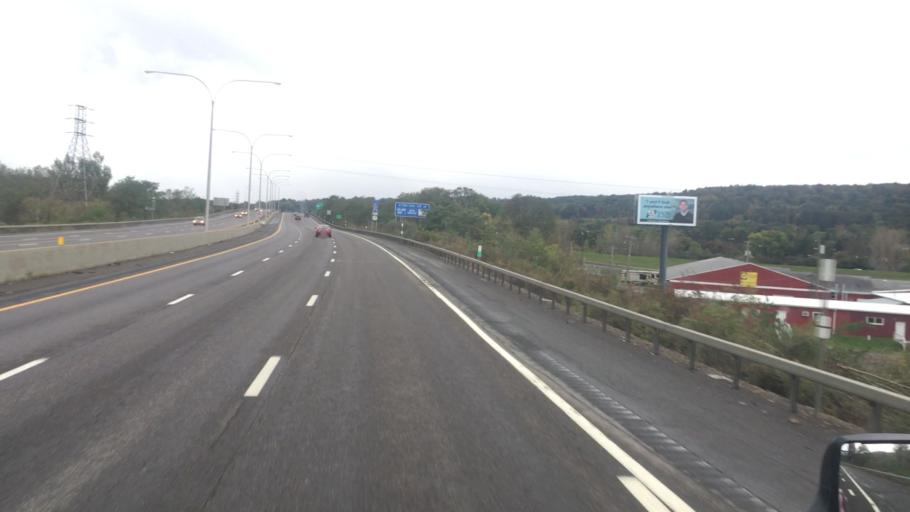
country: US
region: New York
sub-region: Broome County
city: Johnson City
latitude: 42.1202
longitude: -75.9786
